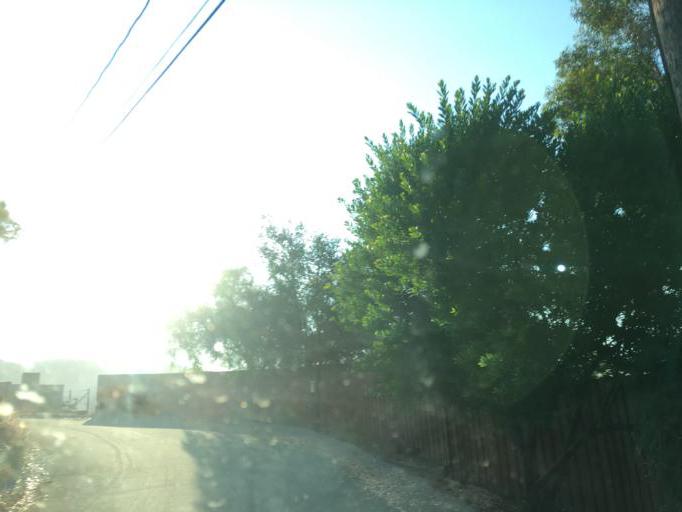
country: US
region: California
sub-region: Los Angeles County
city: Las Flores
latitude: 34.0499
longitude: -118.6446
